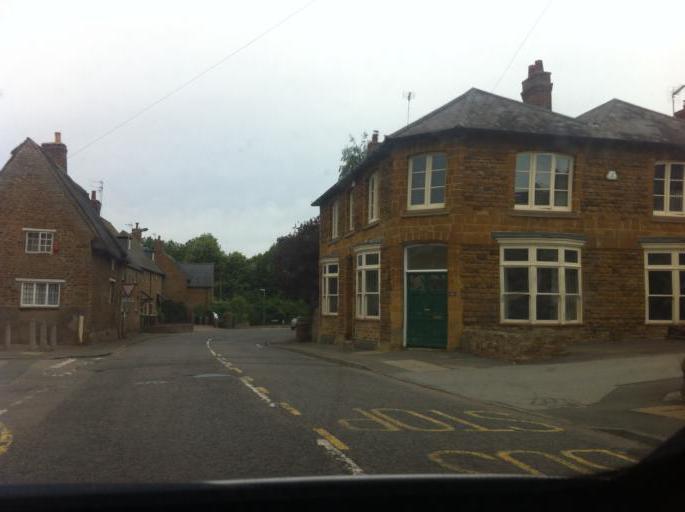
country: GB
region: England
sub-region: Northamptonshire
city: Earls Barton
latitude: 52.2657
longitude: -0.7560
